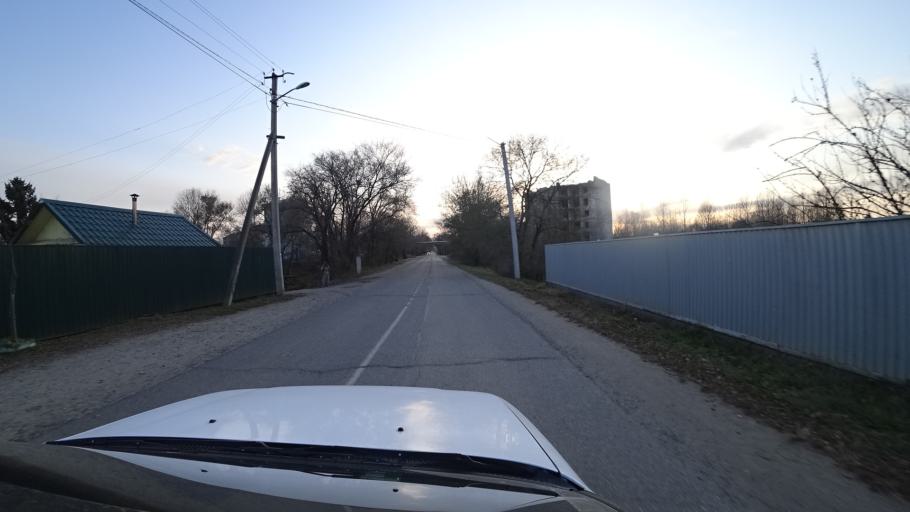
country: RU
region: Primorskiy
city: Dal'nerechensk
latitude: 45.9476
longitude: 133.8197
